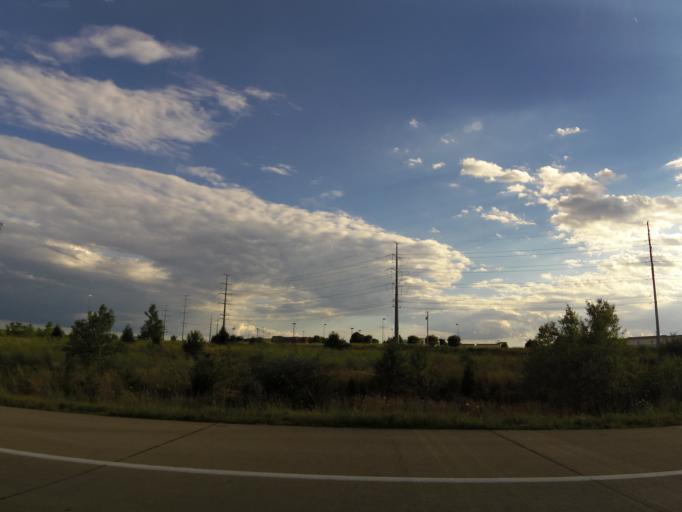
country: US
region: Missouri
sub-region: Saint Charles County
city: Lake Saint Louis
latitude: 38.7727
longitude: -90.7812
